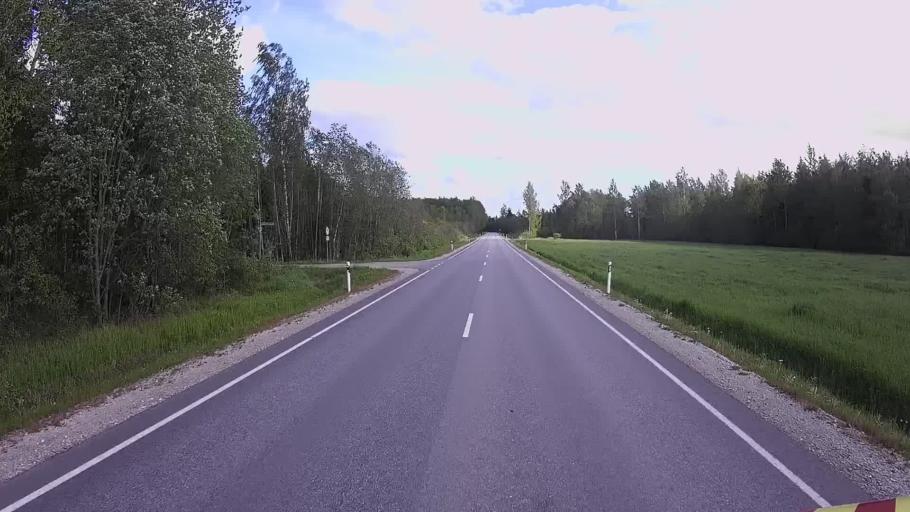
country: EE
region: Jogevamaa
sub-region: Mustvee linn
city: Mustvee
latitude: 58.8774
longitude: 26.8186
